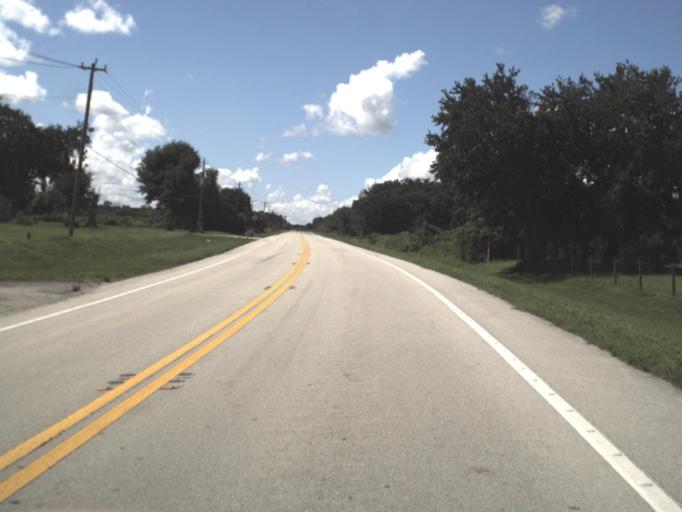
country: US
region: Florida
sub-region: DeSoto County
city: Arcadia
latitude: 27.2310
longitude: -81.8979
